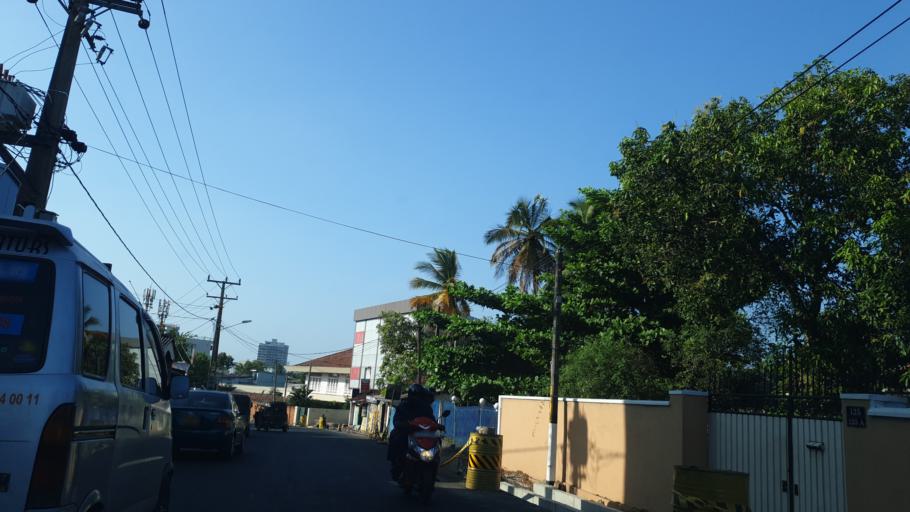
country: LK
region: Western
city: Sri Jayewardenepura Kotte
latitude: 6.8723
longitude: 79.9052
